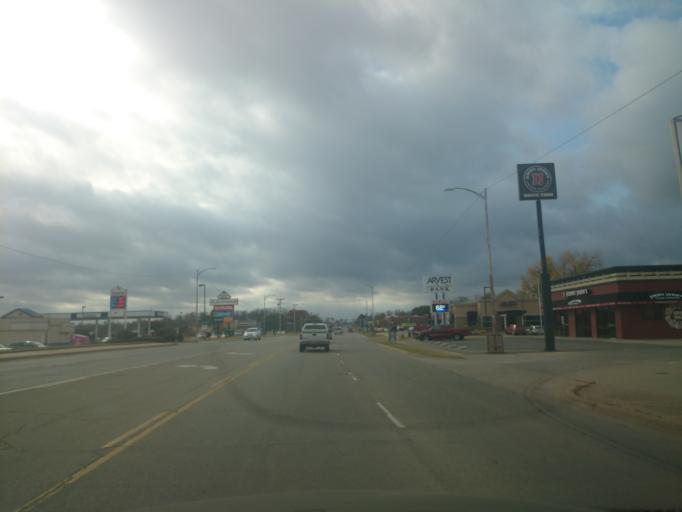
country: US
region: Oklahoma
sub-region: Payne County
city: Stillwater
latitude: 36.1294
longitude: -97.0589
